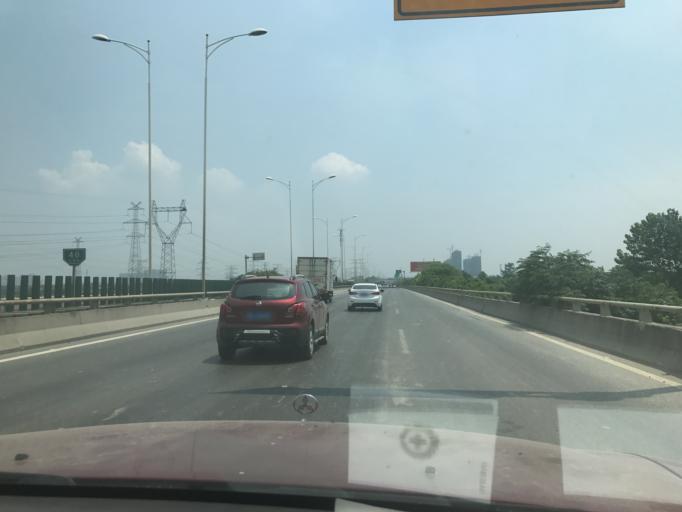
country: CN
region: Hubei
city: Houhu
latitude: 30.6854
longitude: 114.3261
